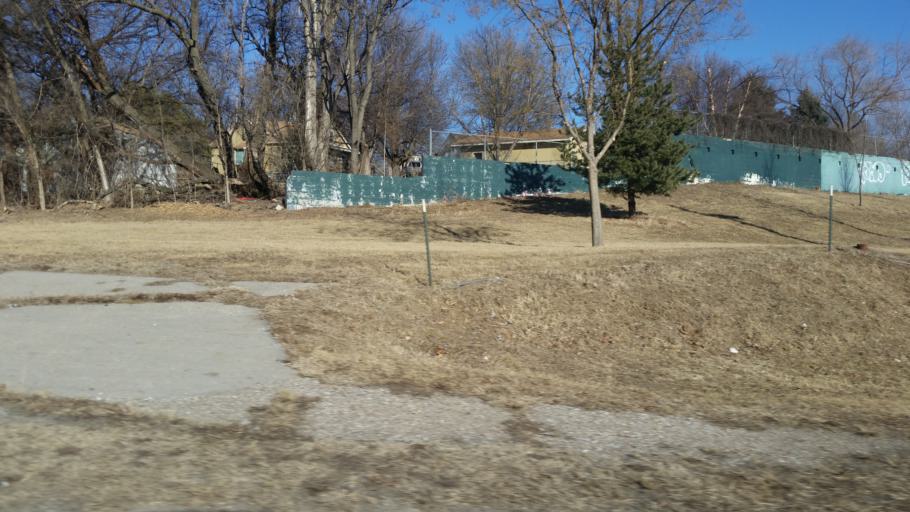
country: US
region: Nebraska
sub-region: Sarpy County
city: Bellevue
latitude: 41.1881
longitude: -95.9333
